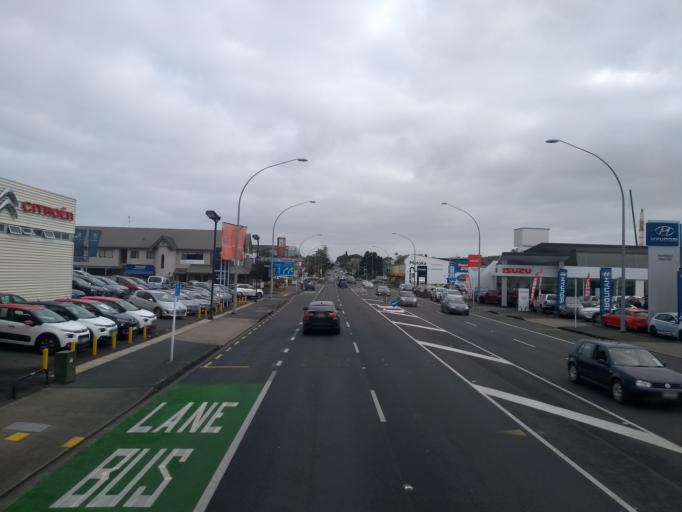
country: NZ
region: Auckland
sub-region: Auckland
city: Auckland
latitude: -36.8919
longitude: 174.7960
